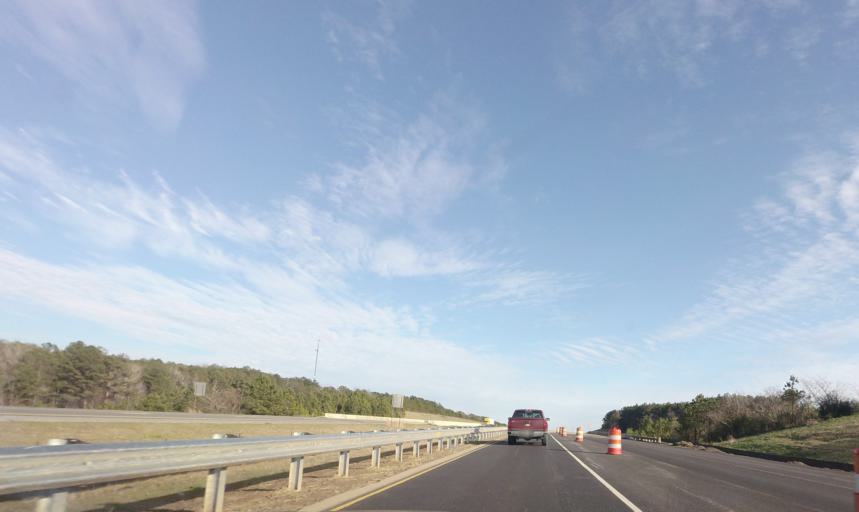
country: US
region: Alabama
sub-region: Walker County
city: Jasper
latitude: 33.8625
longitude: -87.3943
